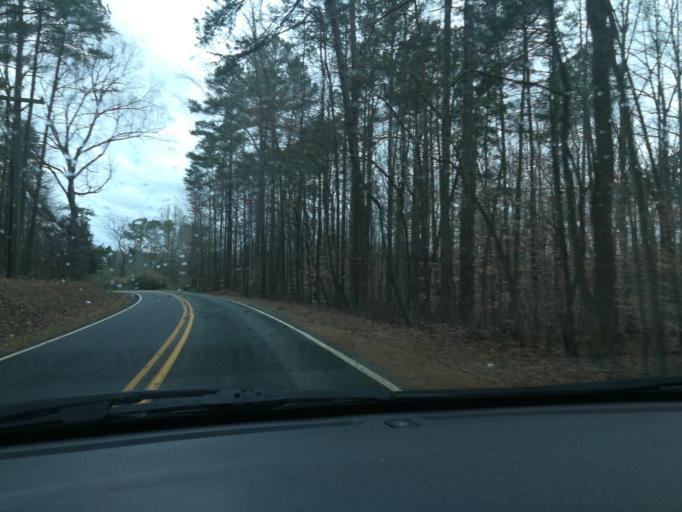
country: US
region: North Carolina
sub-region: Orange County
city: Hillsborough
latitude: 36.0314
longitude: -79.0600
